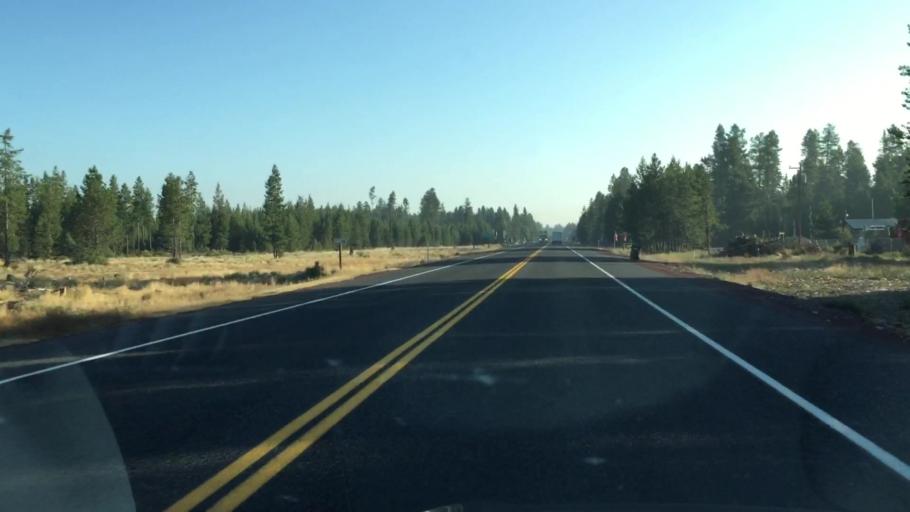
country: US
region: Oregon
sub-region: Deschutes County
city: La Pine
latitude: 43.4501
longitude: -121.7052
